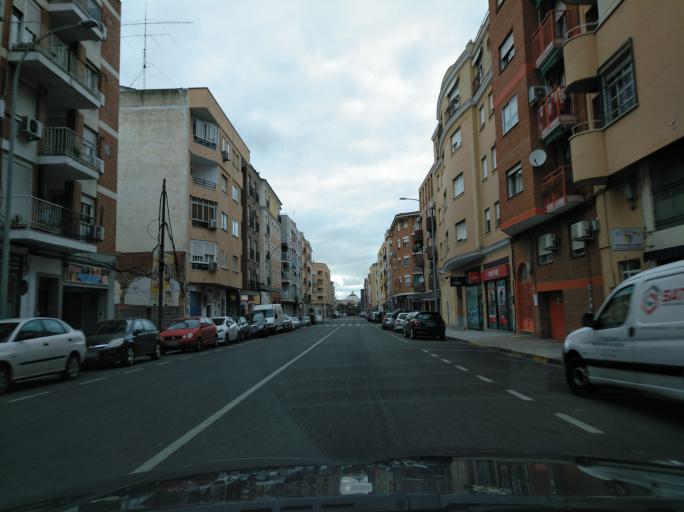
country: ES
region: Extremadura
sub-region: Provincia de Badajoz
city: Badajoz
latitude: 38.8762
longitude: -6.9572
